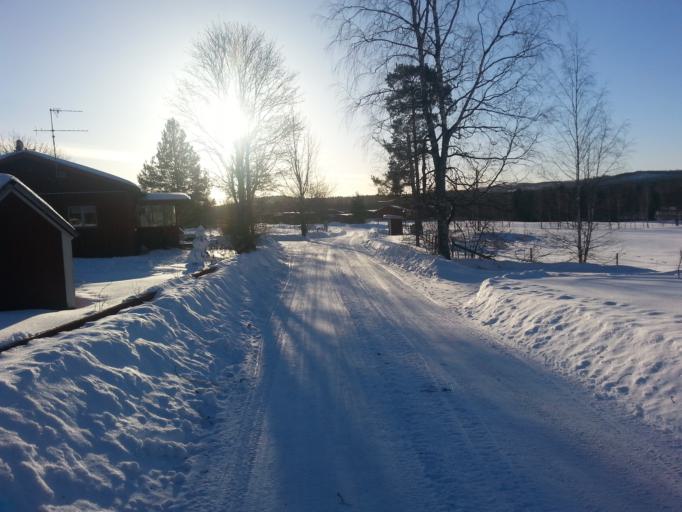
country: SE
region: Dalarna
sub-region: Borlange Kommun
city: Borlaenge
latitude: 60.5762
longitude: 15.4691
